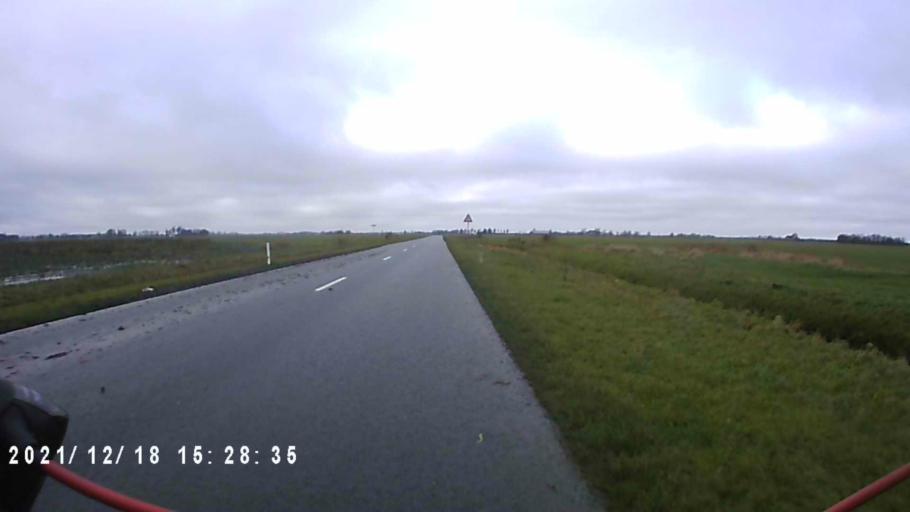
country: NL
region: Friesland
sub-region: Gemeente Dongeradeel
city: Anjum
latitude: 53.3324
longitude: 6.1441
